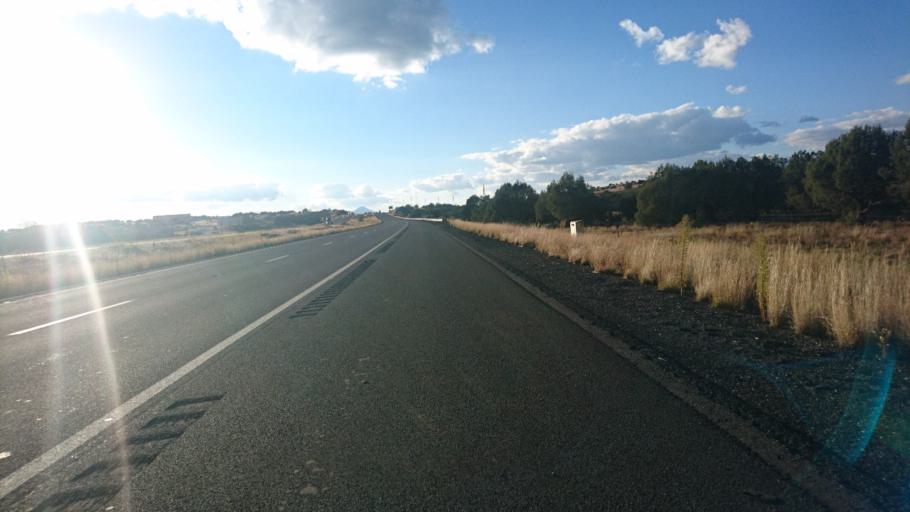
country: US
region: Arizona
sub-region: Coconino County
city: Williams
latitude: 35.2197
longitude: -112.4489
